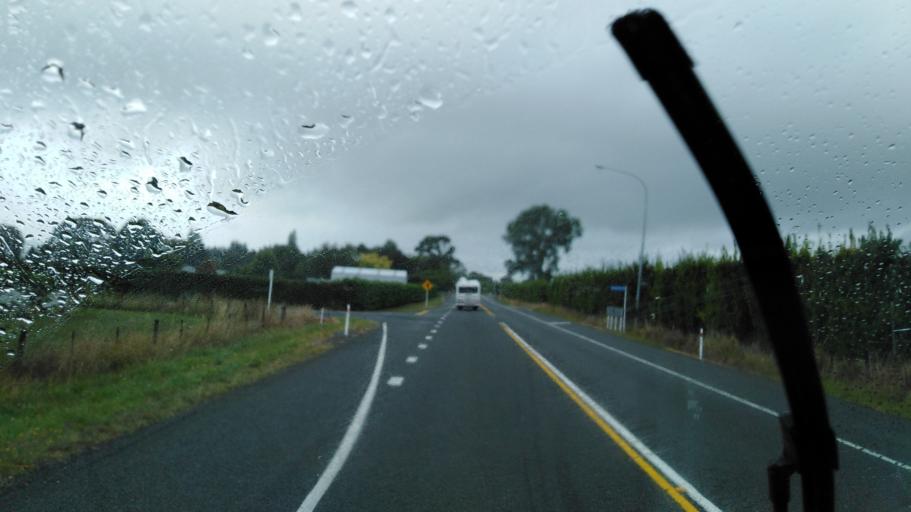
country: NZ
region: Marlborough
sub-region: Marlborough District
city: Blenheim
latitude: -41.4595
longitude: 173.9455
